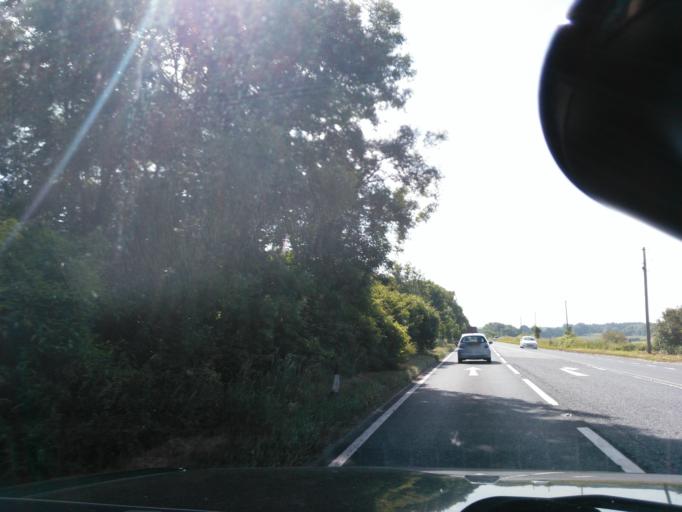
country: GB
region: England
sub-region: Wiltshire
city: Whiteparish
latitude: 51.0183
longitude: -1.6915
